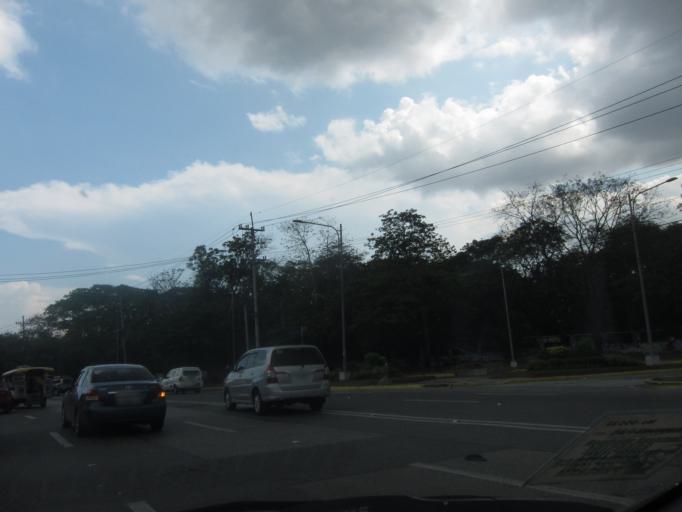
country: PH
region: Metro Manila
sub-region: Quezon City
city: Quezon City
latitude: 14.6522
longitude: 121.0465
